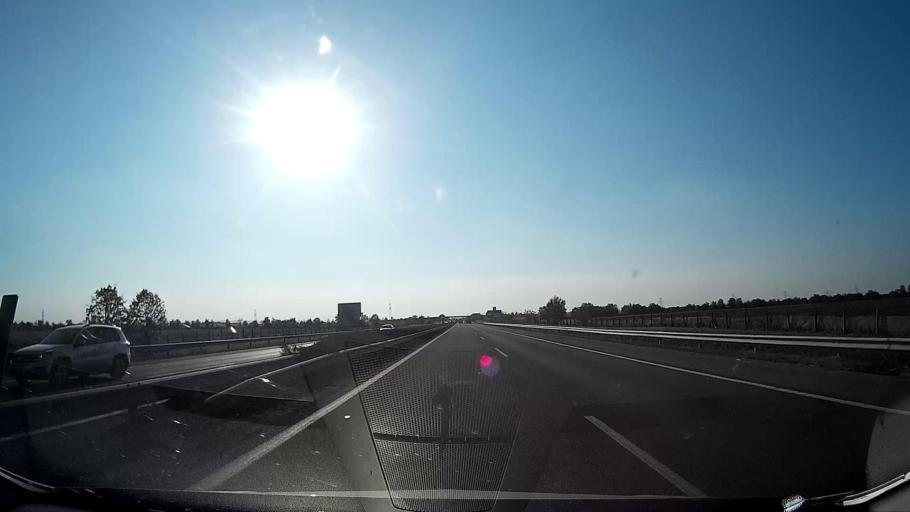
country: HU
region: Gyor-Moson-Sopron
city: Toltestava
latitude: 47.6663
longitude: 17.7612
